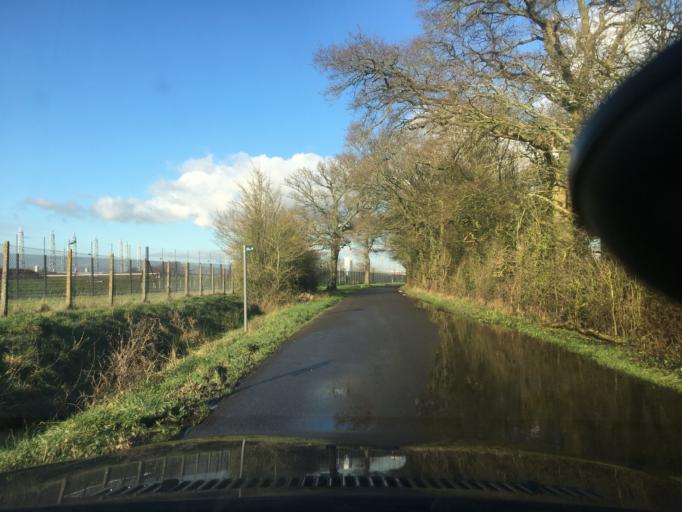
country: GB
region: England
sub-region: West Berkshire
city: Stratfield Mortimer
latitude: 51.4025
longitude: -1.0211
